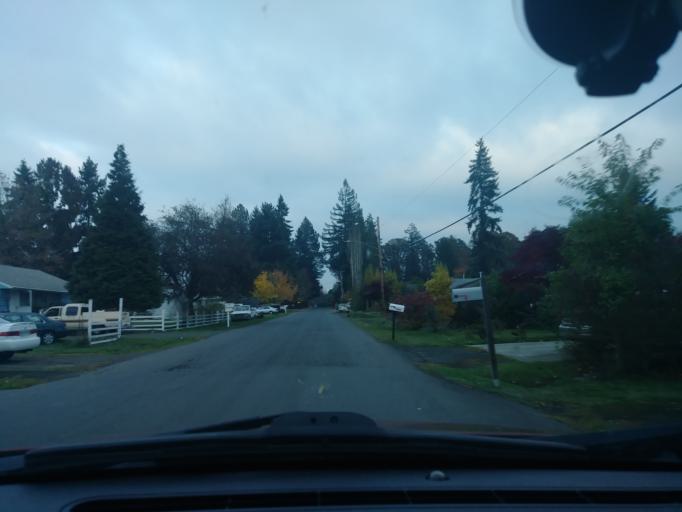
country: US
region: Oregon
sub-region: Washington County
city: Aloha
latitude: 45.4869
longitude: -122.8512
